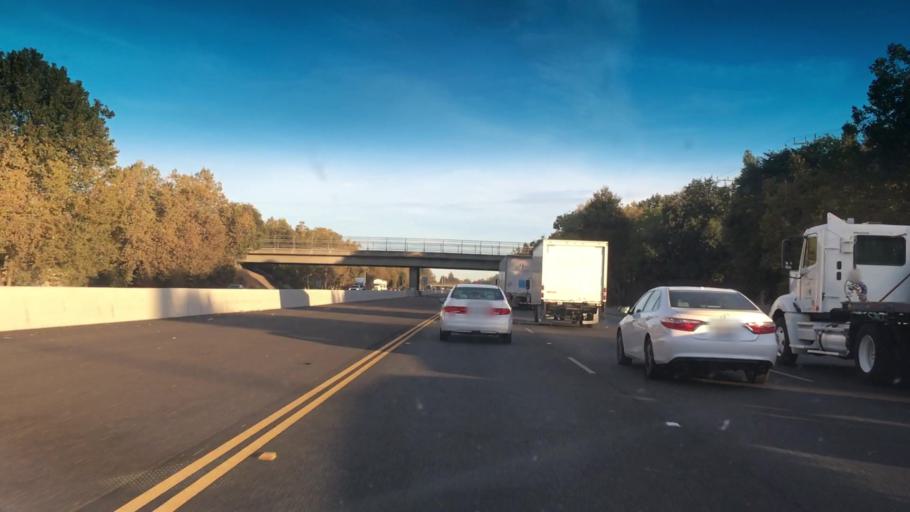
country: US
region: California
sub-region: Sacramento County
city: Parkway
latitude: 38.4876
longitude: -121.5132
